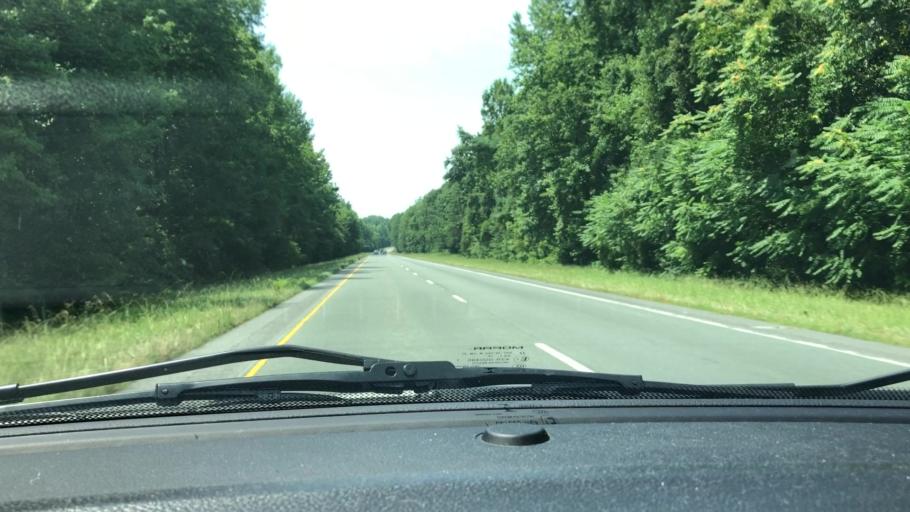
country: US
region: North Carolina
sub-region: Randolph County
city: Liberty
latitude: 35.8588
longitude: -79.6167
